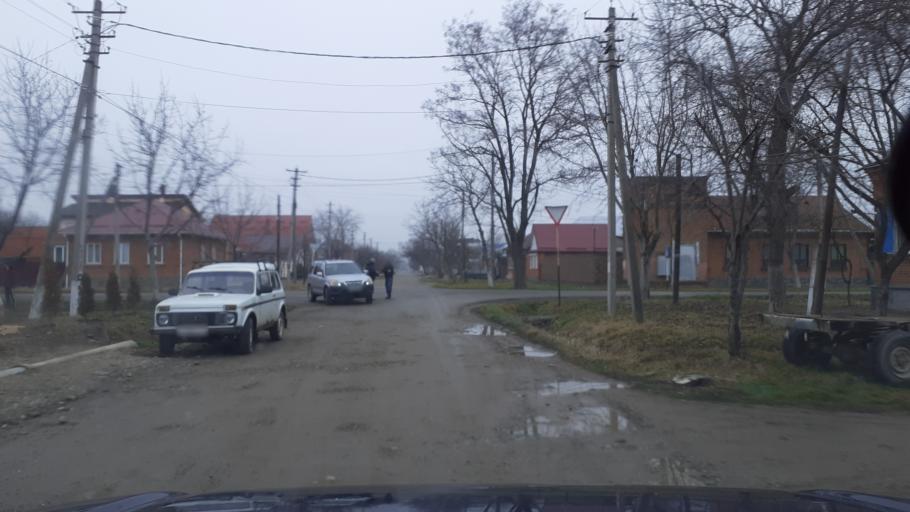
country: RU
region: Adygeya
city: Maykop
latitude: 44.6175
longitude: 40.0879
